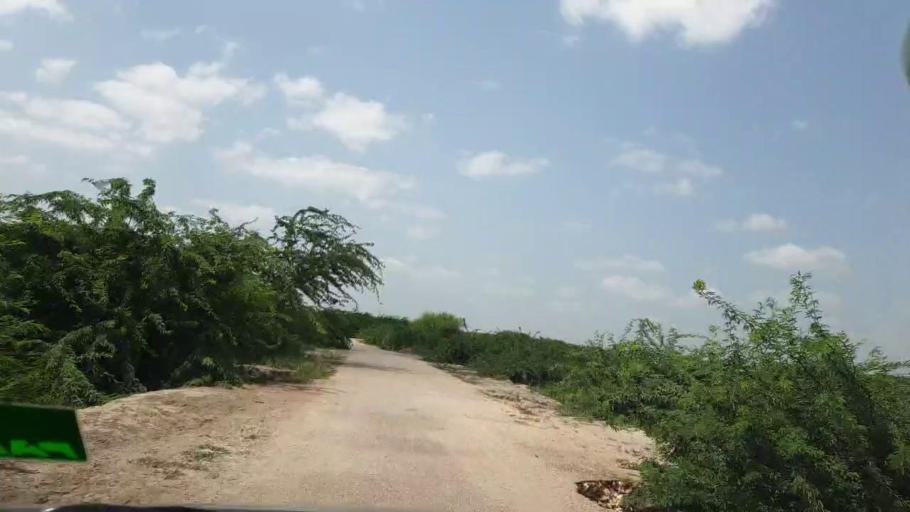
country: PK
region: Sindh
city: Kadhan
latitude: 24.5517
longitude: 69.1877
